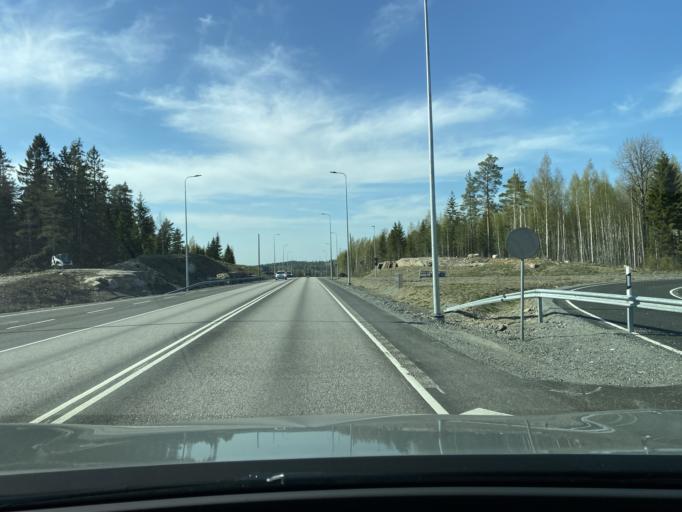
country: FI
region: Uusimaa
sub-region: Helsinki
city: Nurmijaervi
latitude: 60.3892
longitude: 24.7842
